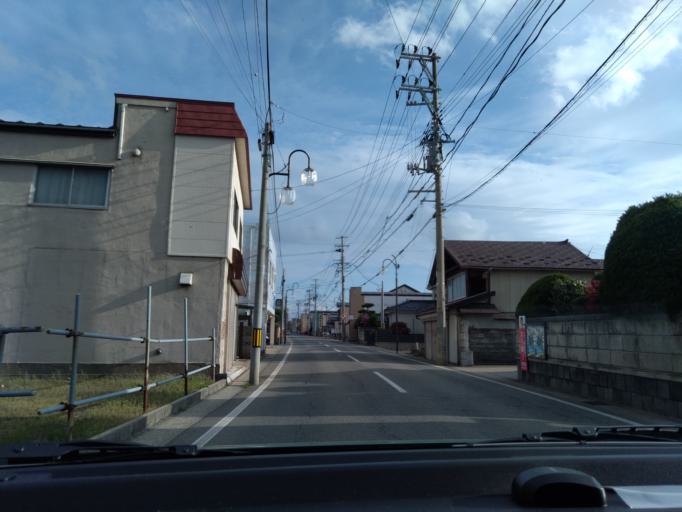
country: JP
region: Akita
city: Akita Shi
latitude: 39.7627
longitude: 140.0694
